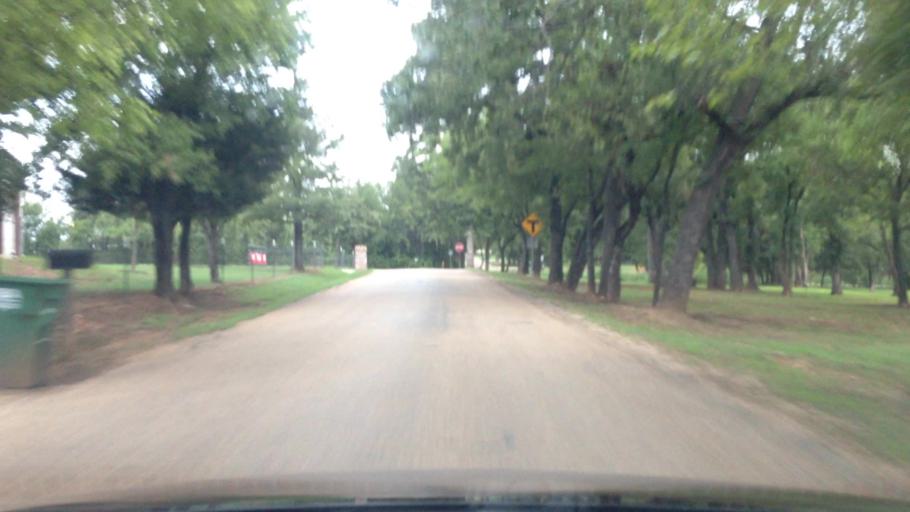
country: US
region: Texas
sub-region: Johnson County
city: Joshua
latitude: 32.4786
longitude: -97.3361
